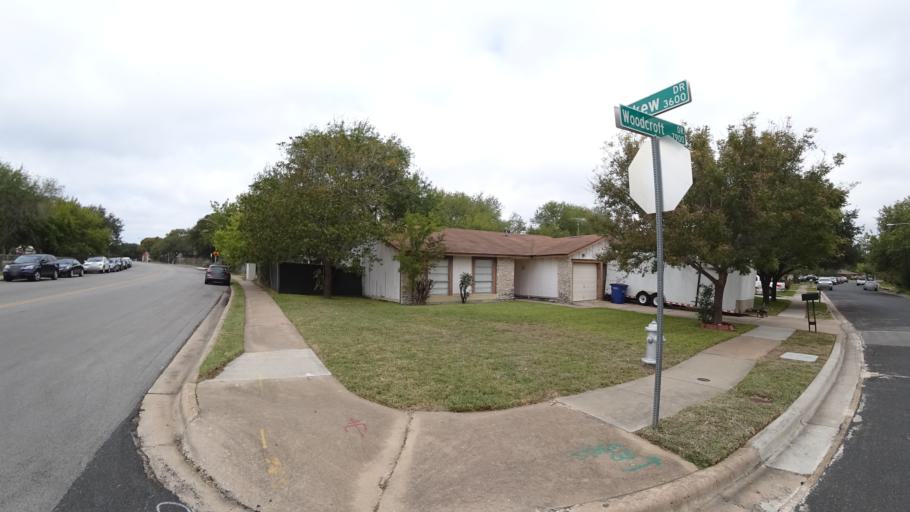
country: US
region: Texas
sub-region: Travis County
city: Shady Hollow
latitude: 30.2047
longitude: -97.8389
